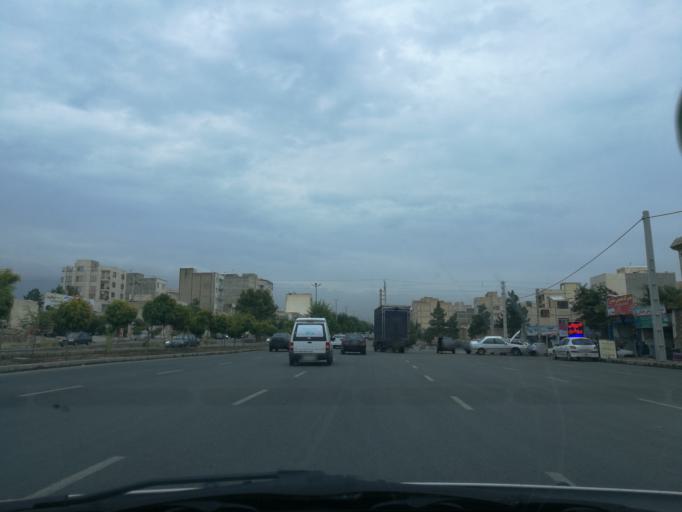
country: IR
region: Alborz
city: Karaj
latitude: 35.8615
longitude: 50.9377
